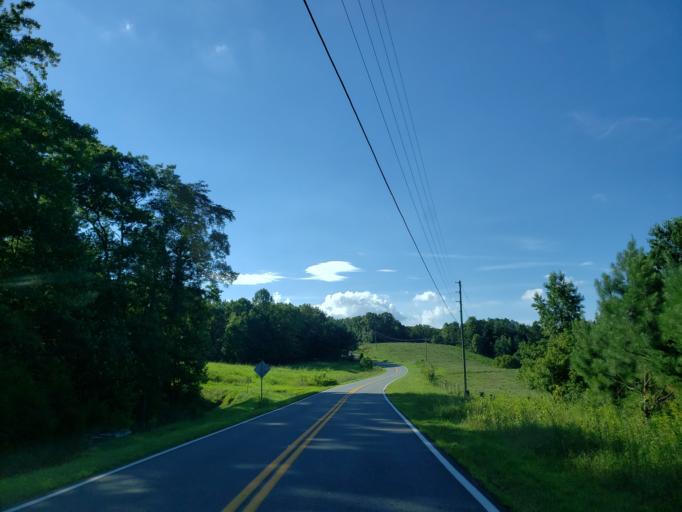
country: US
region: Georgia
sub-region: Bartow County
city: Rydal
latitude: 34.3500
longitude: -84.5981
